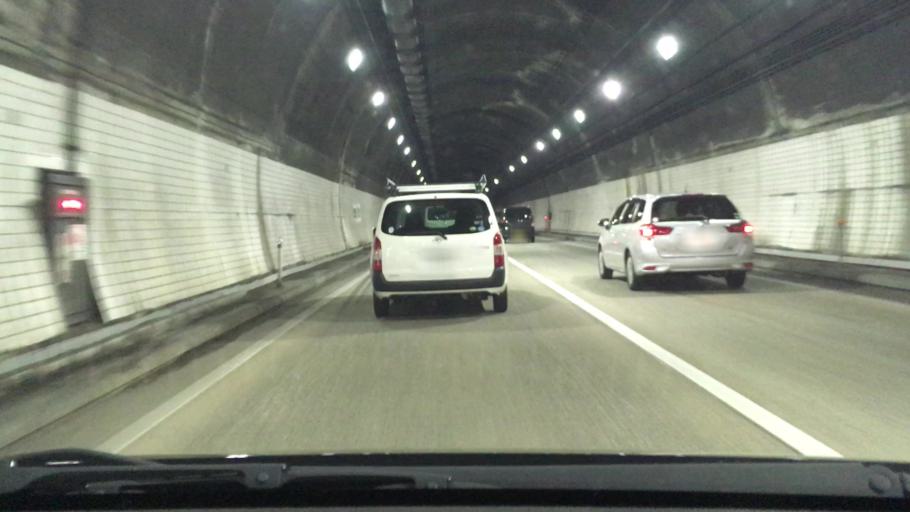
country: JP
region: Hiroshima
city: Hiroshima-shi
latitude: 34.3837
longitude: 132.3935
